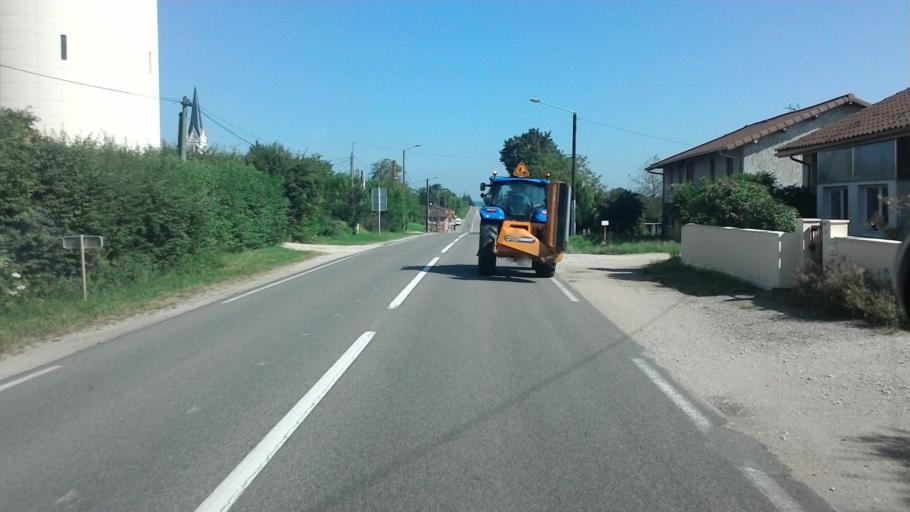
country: FR
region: Rhone-Alpes
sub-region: Departement de l'Ain
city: Montrevel-en-Bresse
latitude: 46.3664
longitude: 5.1213
